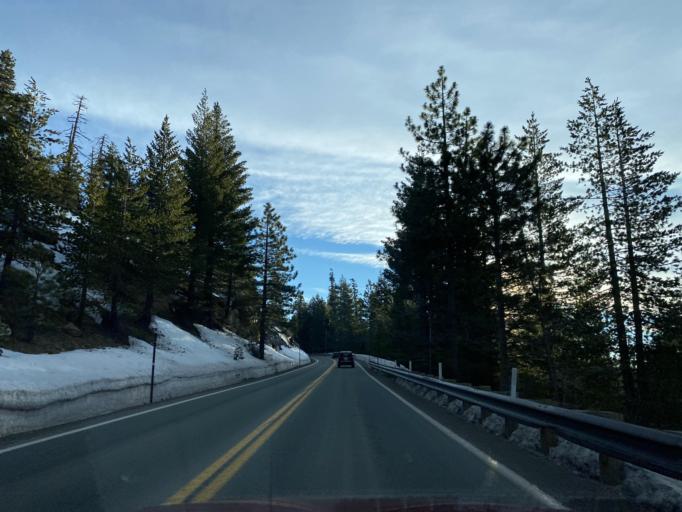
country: US
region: California
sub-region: Amador County
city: Pioneer
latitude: 38.5452
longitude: -120.3341
